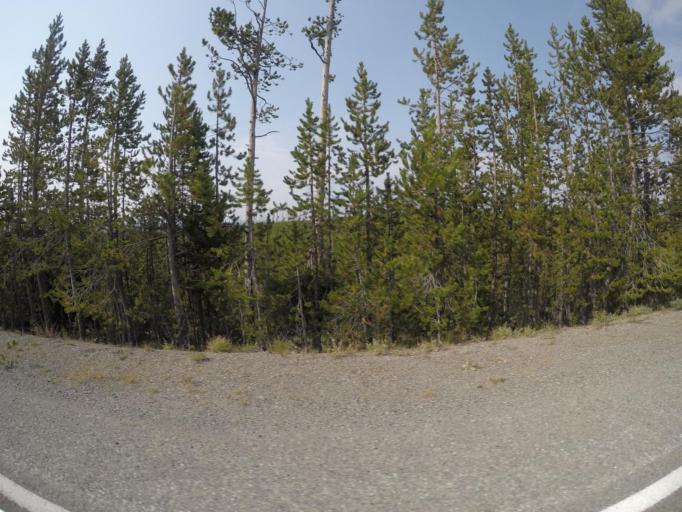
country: US
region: Montana
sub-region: Gallatin County
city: West Yellowstone
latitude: 44.7197
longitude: -110.6502
